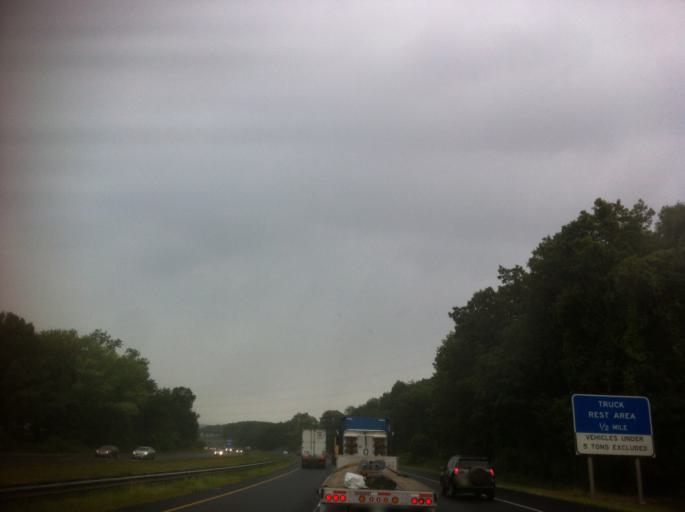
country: US
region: New Jersey
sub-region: Morris County
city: Rockaway
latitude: 40.9113
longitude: -74.5159
